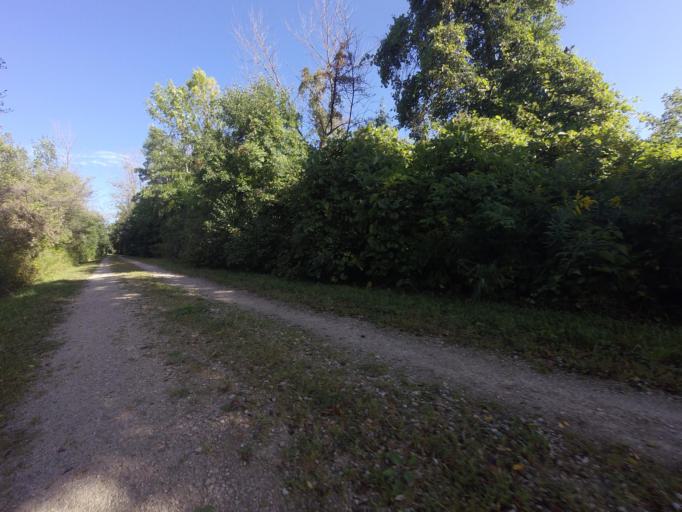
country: CA
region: Ontario
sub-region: Wellington County
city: Guelph
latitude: 43.6617
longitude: -80.4310
